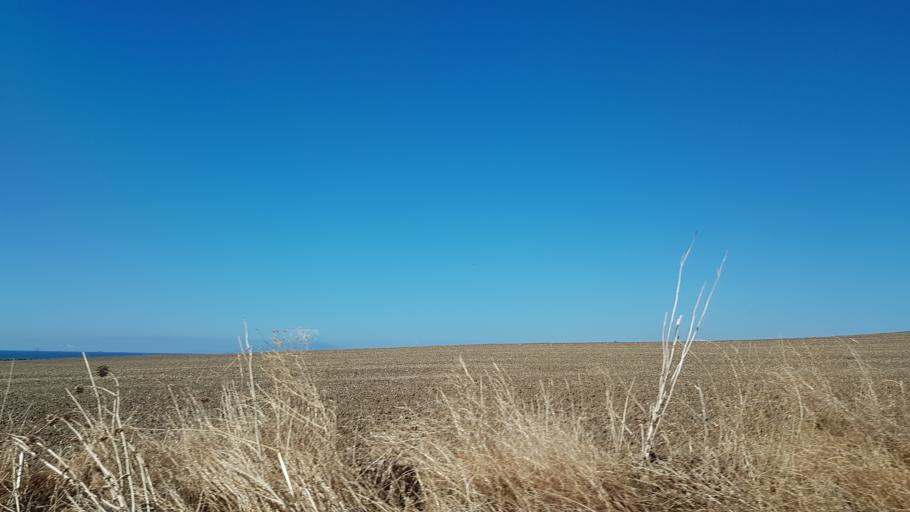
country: TR
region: Tekirdag
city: Corlu
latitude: 41.0174
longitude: 27.8066
